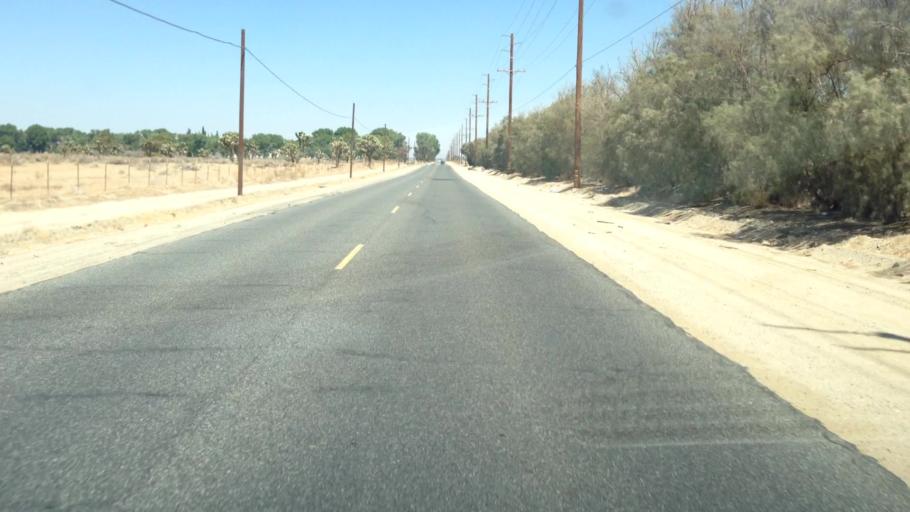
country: US
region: California
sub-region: Los Angeles County
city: Palmdale
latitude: 34.5916
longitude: -118.0585
